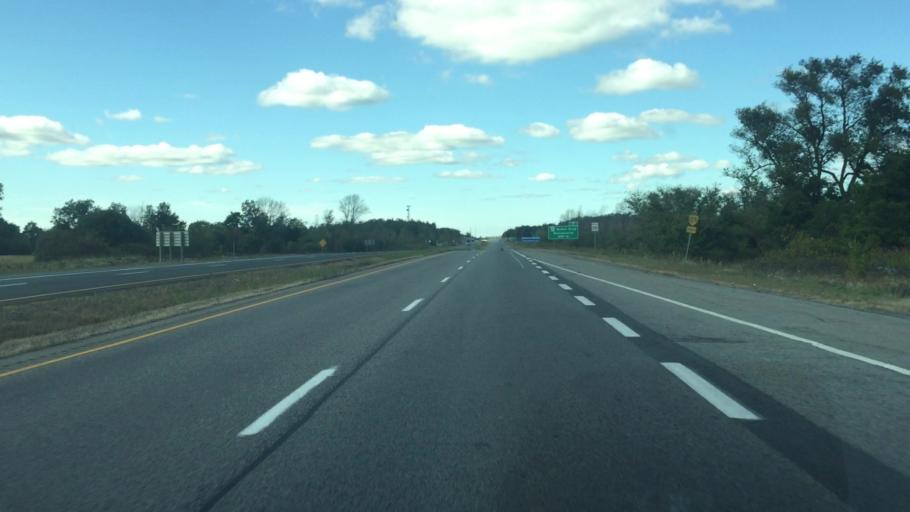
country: CA
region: Ontario
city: Fort Erie
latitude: 42.9237
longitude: -78.9728
